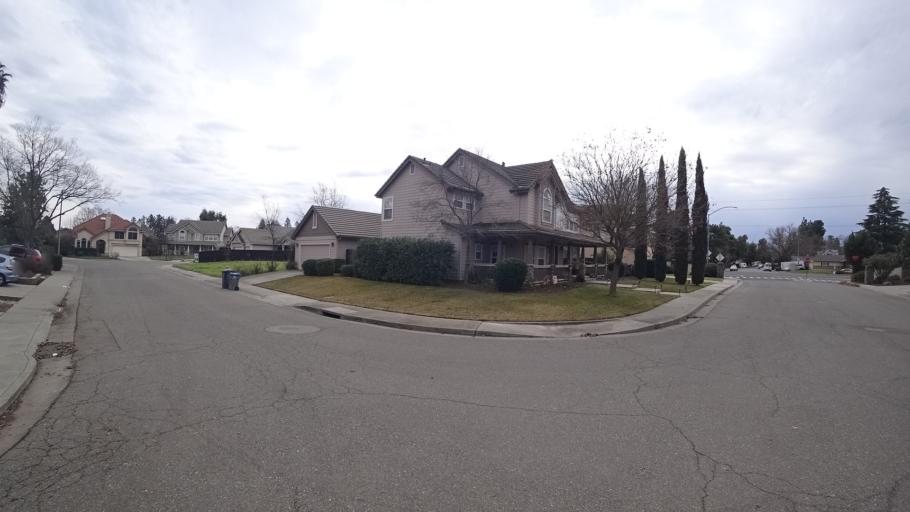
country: US
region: California
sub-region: Yolo County
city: Davis
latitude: 38.5636
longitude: -121.7243
